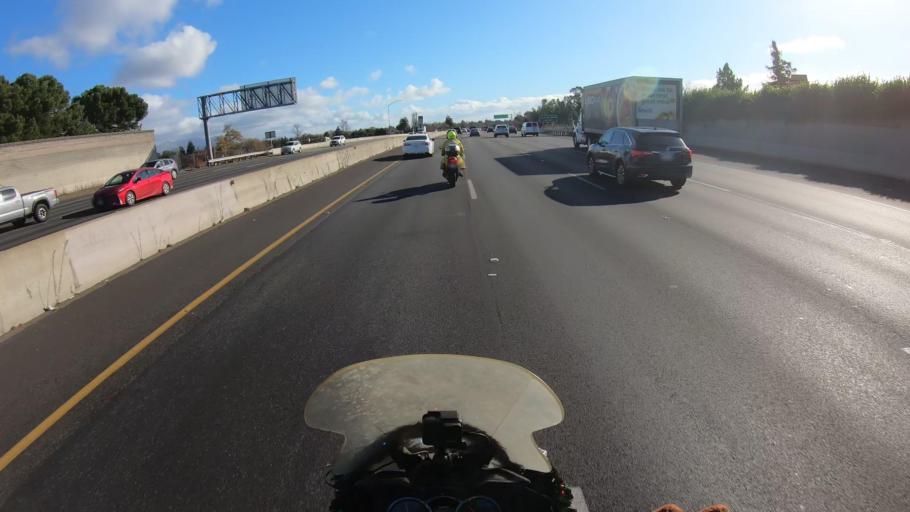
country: US
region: California
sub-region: Alameda County
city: Union City
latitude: 37.5821
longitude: -122.0620
